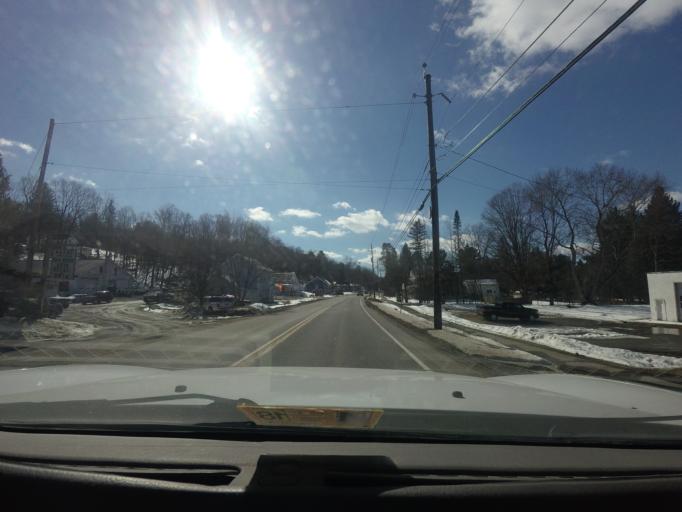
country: US
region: New York
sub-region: Washington County
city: Cambridge
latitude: 43.1683
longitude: -73.3270
